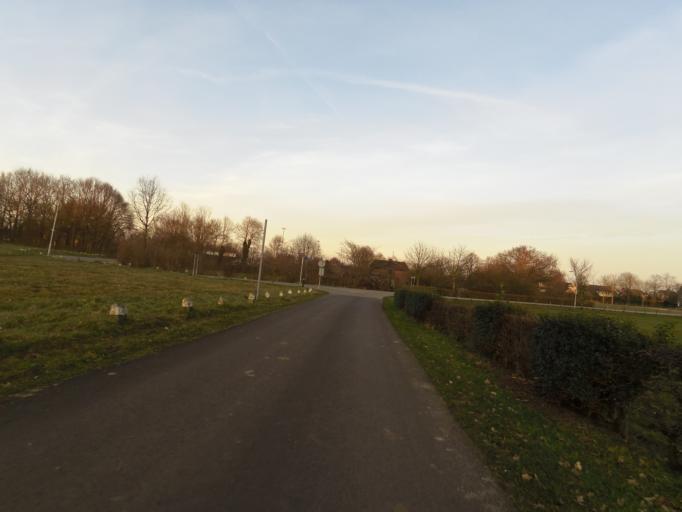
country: NL
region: Gelderland
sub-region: Gemeente Zevenaar
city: Zevenaar
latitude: 51.9403
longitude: 6.1182
